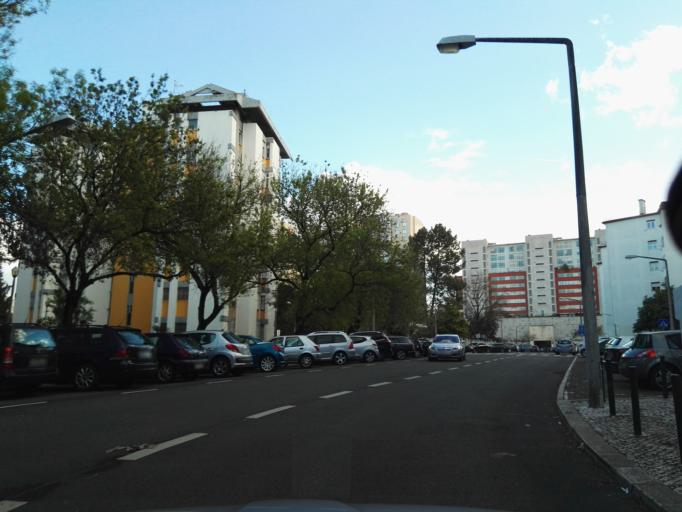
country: PT
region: Lisbon
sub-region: Loures
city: Moscavide
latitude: 38.7647
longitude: -9.1141
